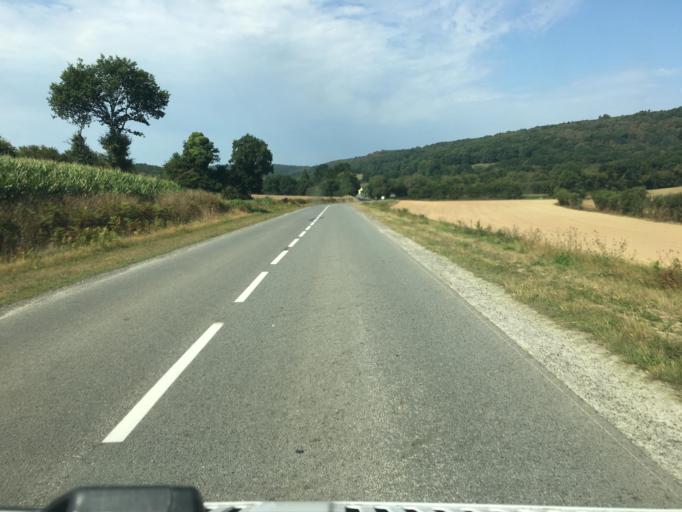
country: FR
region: Brittany
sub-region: Departement des Cotes-d'Armor
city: Gouarec
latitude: 48.2135
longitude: -3.1167
